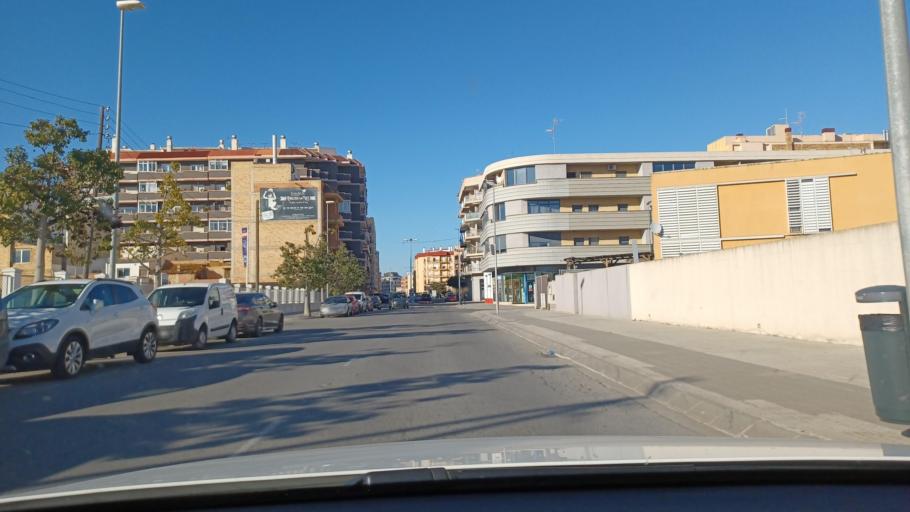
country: ES
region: Catalonia
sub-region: Provincia de Tarragona
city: Amposta
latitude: 40.7015
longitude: 0.5799
